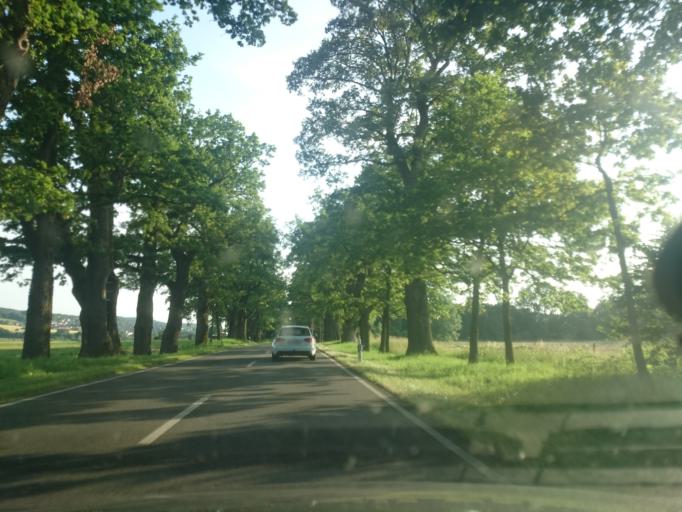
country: DE
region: Bavaria
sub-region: Upper Bavaria
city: Seefeld
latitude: 48.0546
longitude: 11.2303
